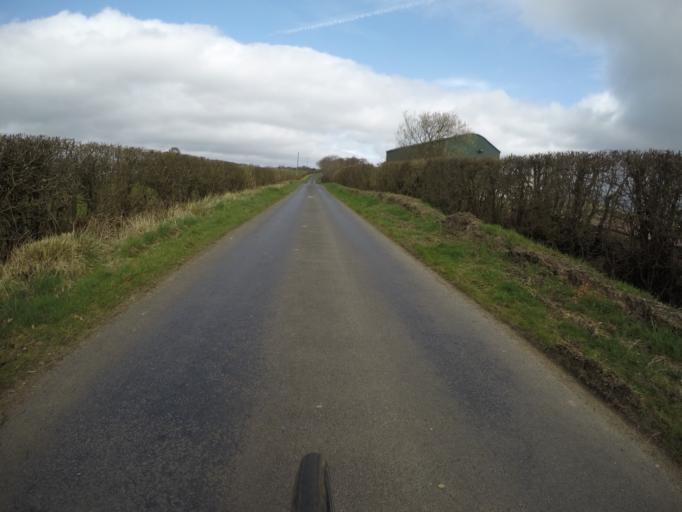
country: GB
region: Scotland
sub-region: North Ayrshire
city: Springside
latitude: 55.6558
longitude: -4.6099
